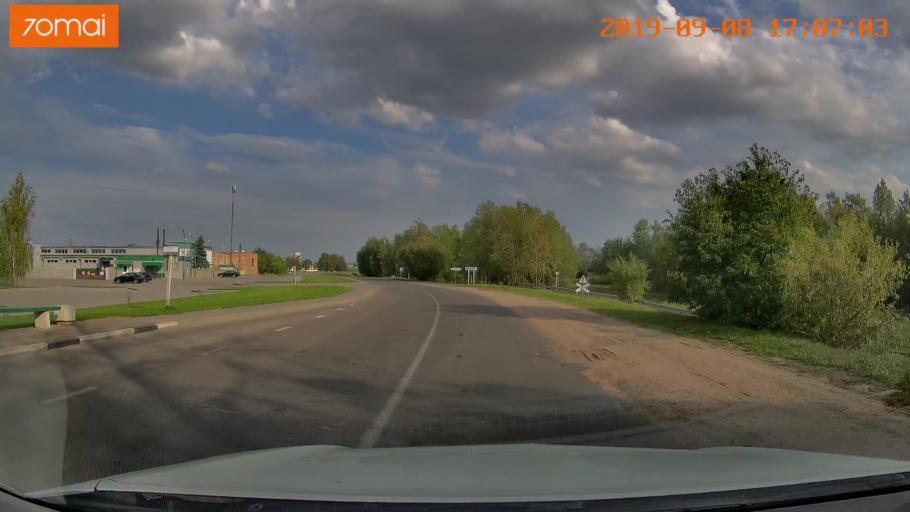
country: BY
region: Grodnenskaya
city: Hrodna
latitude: 53.6660
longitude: 23.9557
